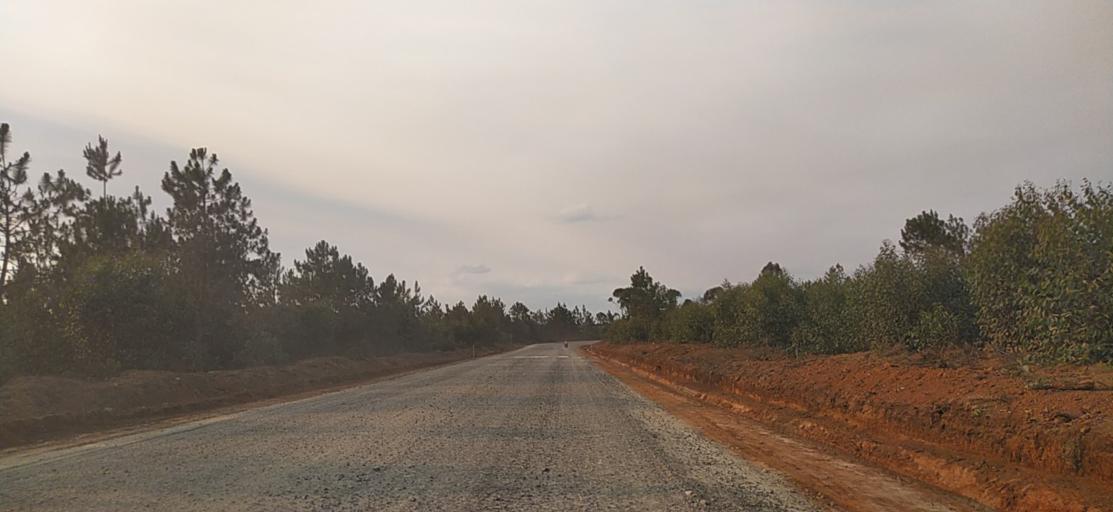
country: MG
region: Alaotra Mangoro
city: Moramanga
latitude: -18.5569
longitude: 48.2586
